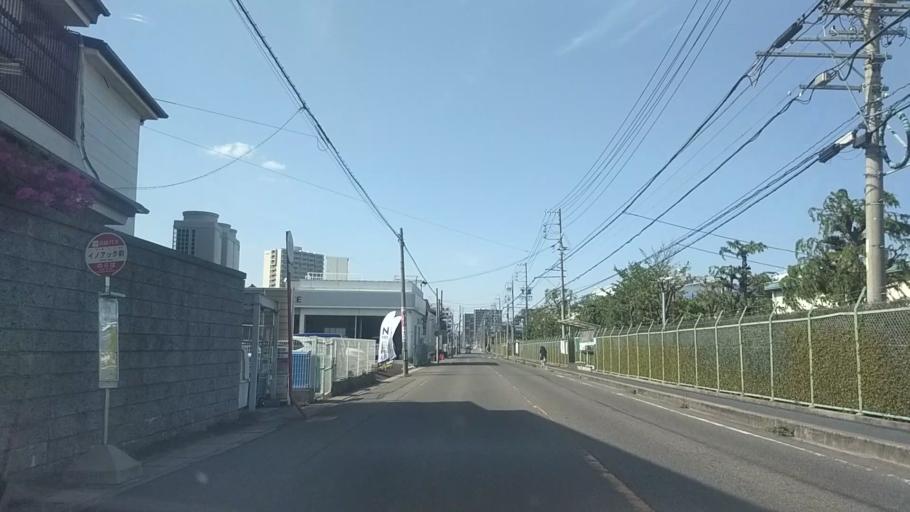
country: JP
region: Aichi
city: Anjo
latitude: 34.9781
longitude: 137.0845
